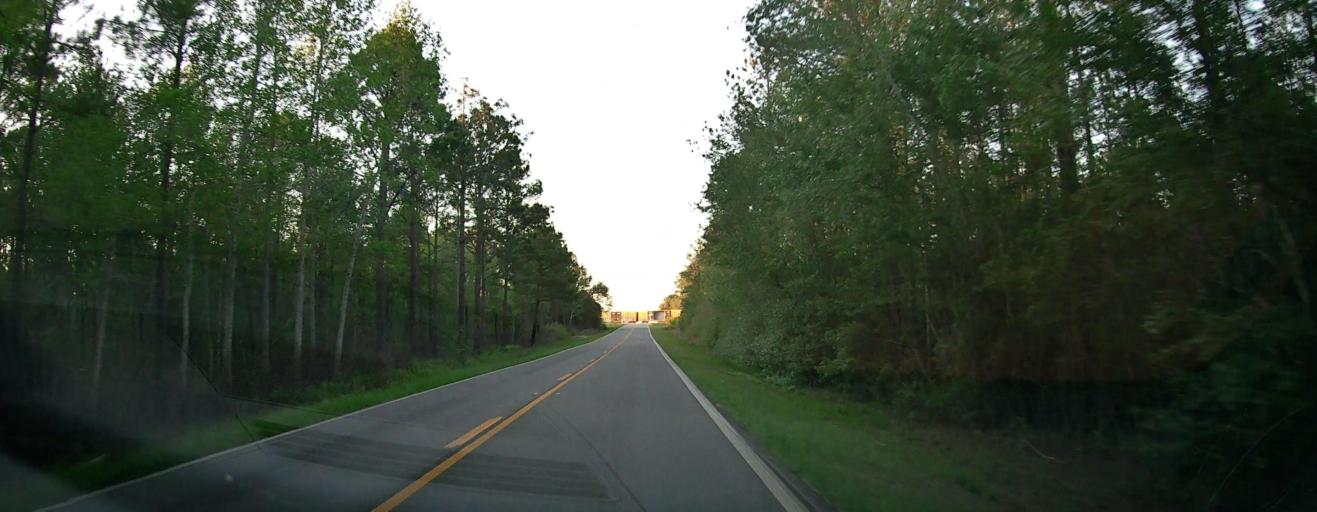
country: US
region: Georgia
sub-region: Ben Hill County
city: Fitzgerald
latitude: 31.7371
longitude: -83.3098
